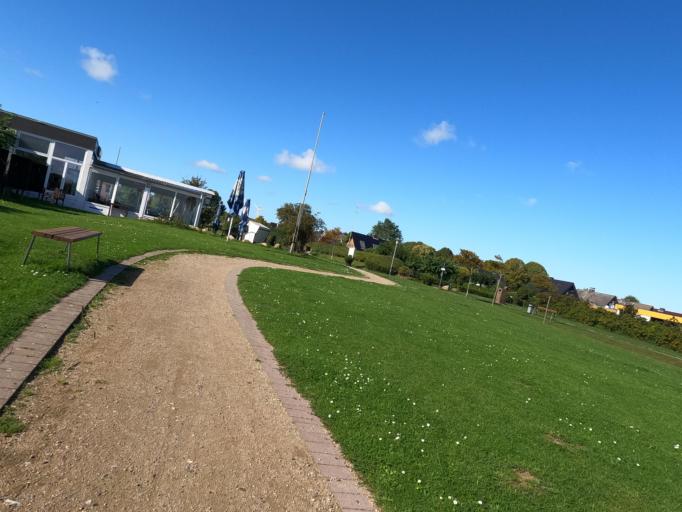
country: DE
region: Schleswig-Holstein
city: Neukirchen
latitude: 54.3061
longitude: 11.0748
